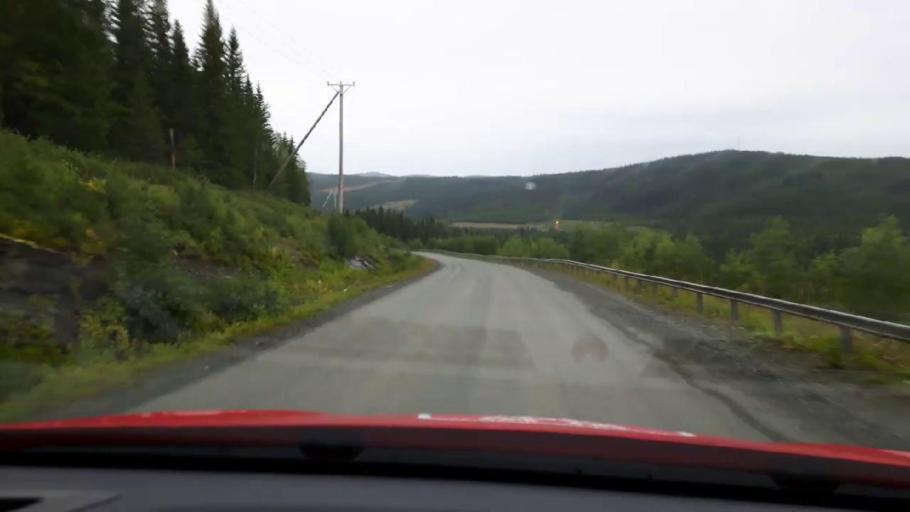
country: SE
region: Jaemtland
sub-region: Are Kommun
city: Are
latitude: 63.4055
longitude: 12.8329
